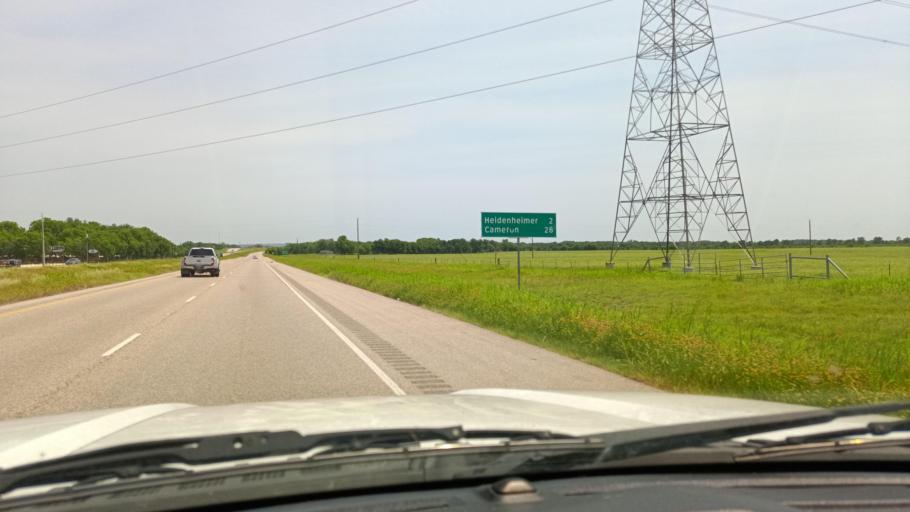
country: US
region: Texas
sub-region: Bell County
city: Temple
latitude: 31.0469
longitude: -97.3245
